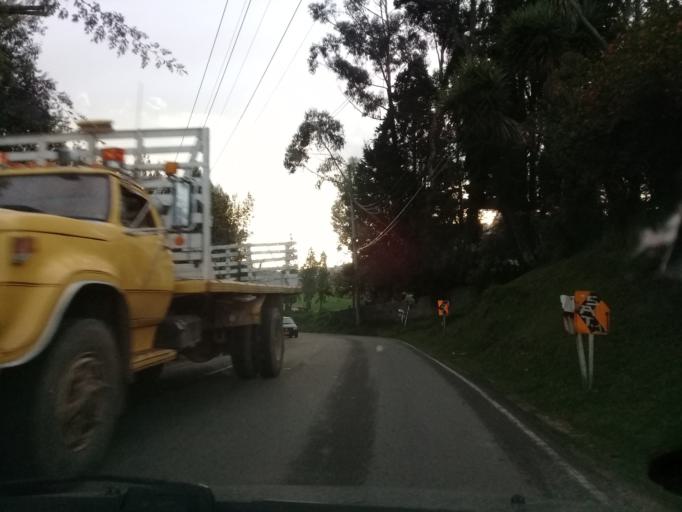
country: CO
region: Cundinamarca
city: Tabio
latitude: 4.9260
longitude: -74.0774
